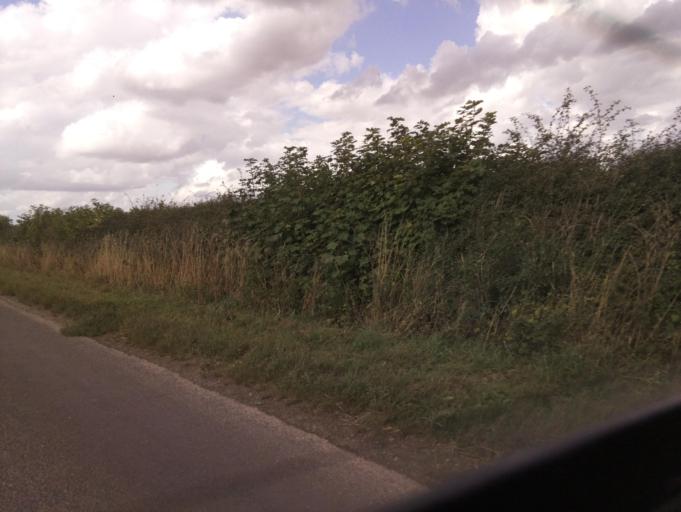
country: GB
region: England
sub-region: North Yorkshire
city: Ripon
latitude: 54.1643
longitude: -1.5477
